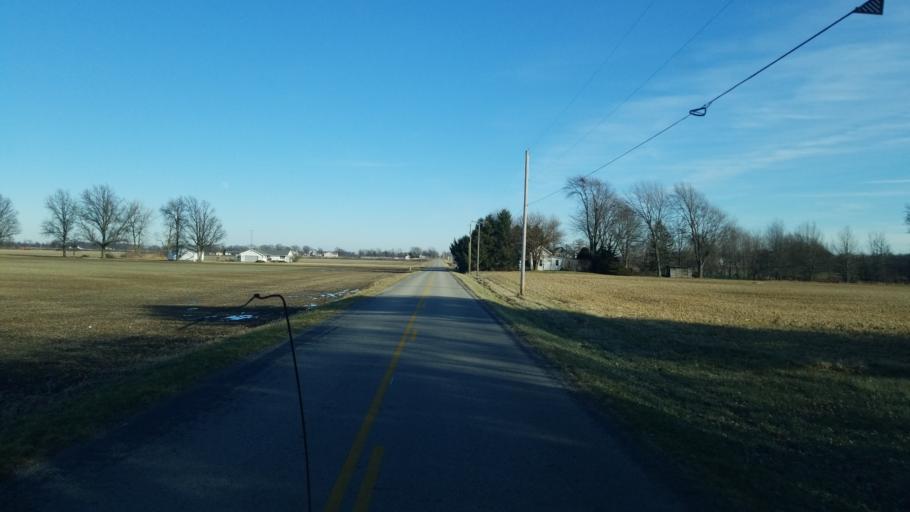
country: US
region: Ohio
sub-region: Sandusky County
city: Mount Carmel
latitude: 41.2561
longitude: -82.9553
